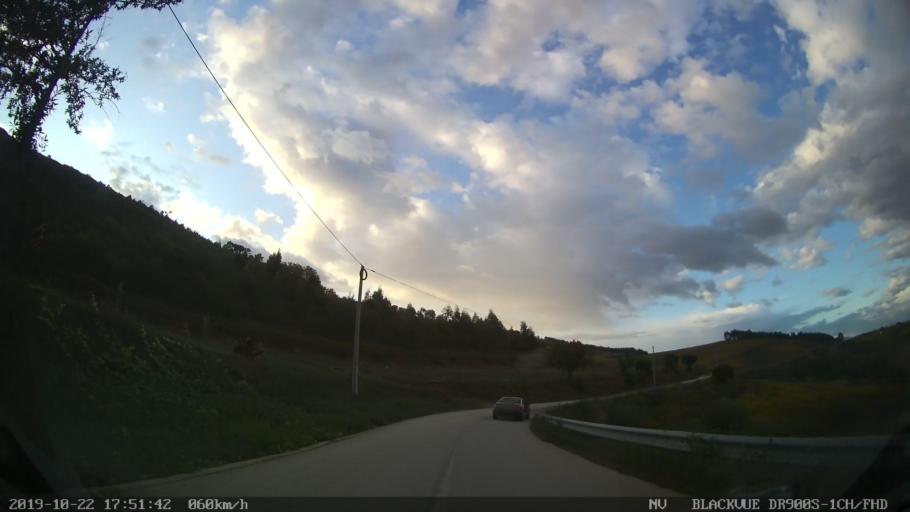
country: PT
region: Vila Real
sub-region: Sabrosa
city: Vilela
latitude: 41.2308
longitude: -7.5691
